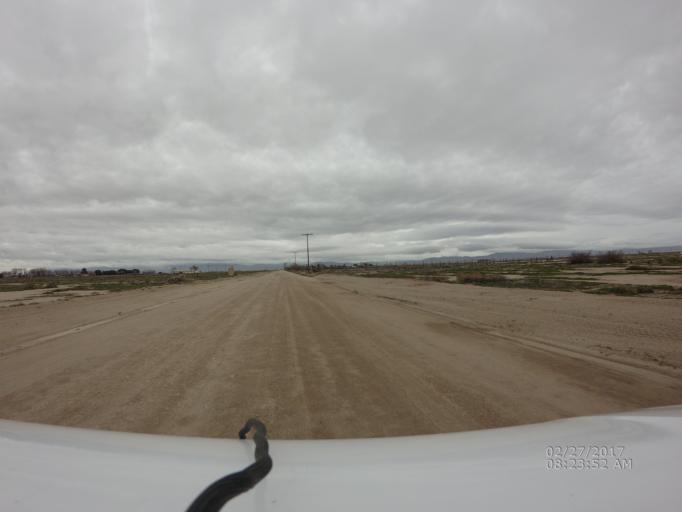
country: US
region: California
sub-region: Los Angeles County
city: Lancaster
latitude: 34.7235
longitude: -118.0144
